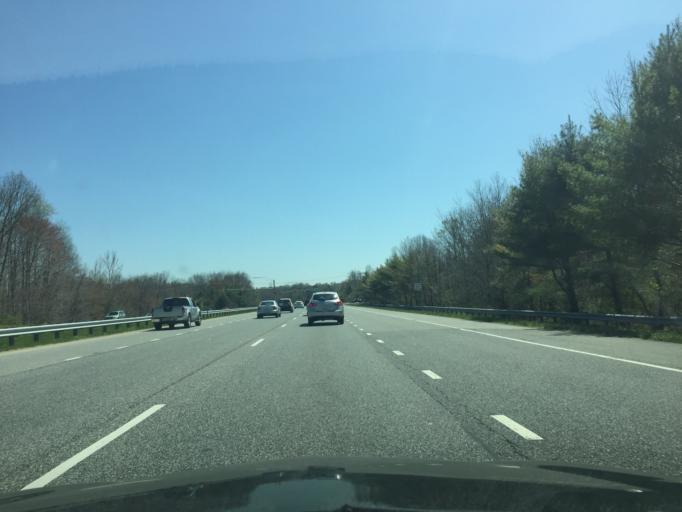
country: US
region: Maryland
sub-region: Harford County
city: South Bel Air
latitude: 39.5132
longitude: -76.3423
